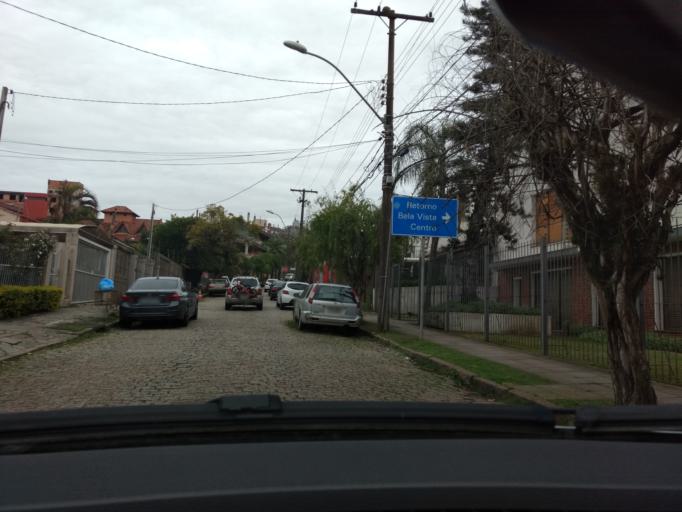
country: BR
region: Rio Grande do Sul
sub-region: Porto Alegre
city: Porto Alegre
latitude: -30.0290
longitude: -51.1698
